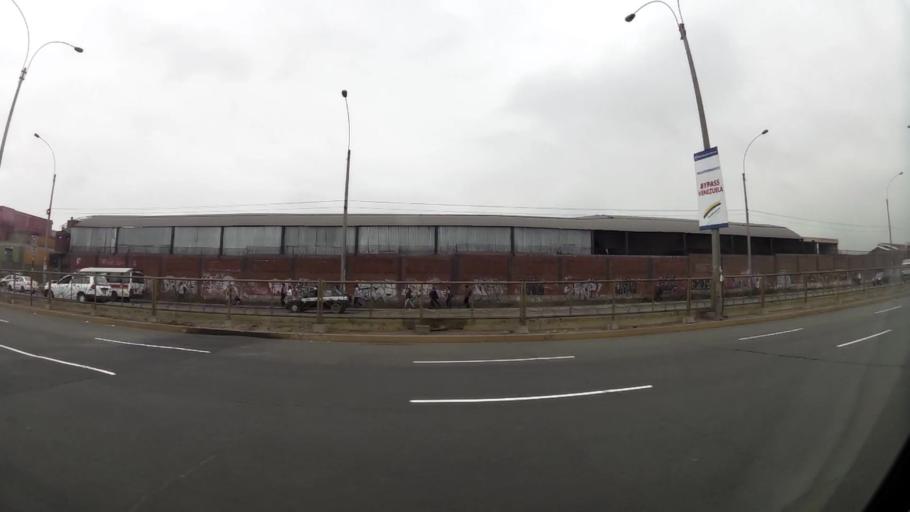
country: PE
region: Callao
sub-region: Callao
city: Callao
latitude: -12.0597
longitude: -77.0769
